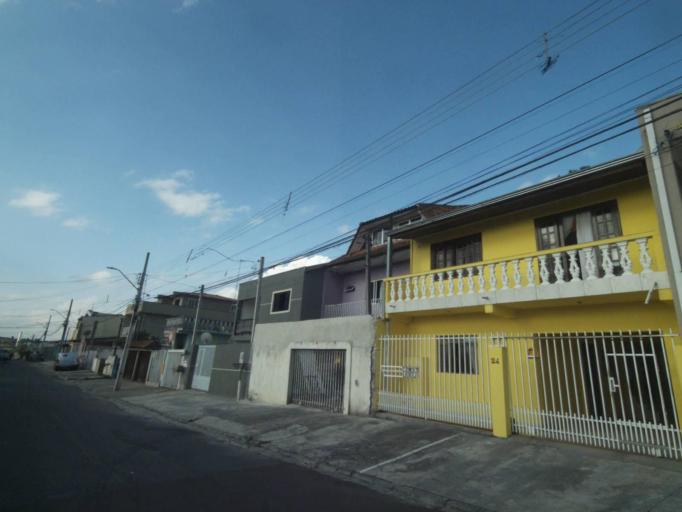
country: BR
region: Parana
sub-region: Araucaria
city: Araucaria
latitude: -25.5295
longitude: -49.3351
